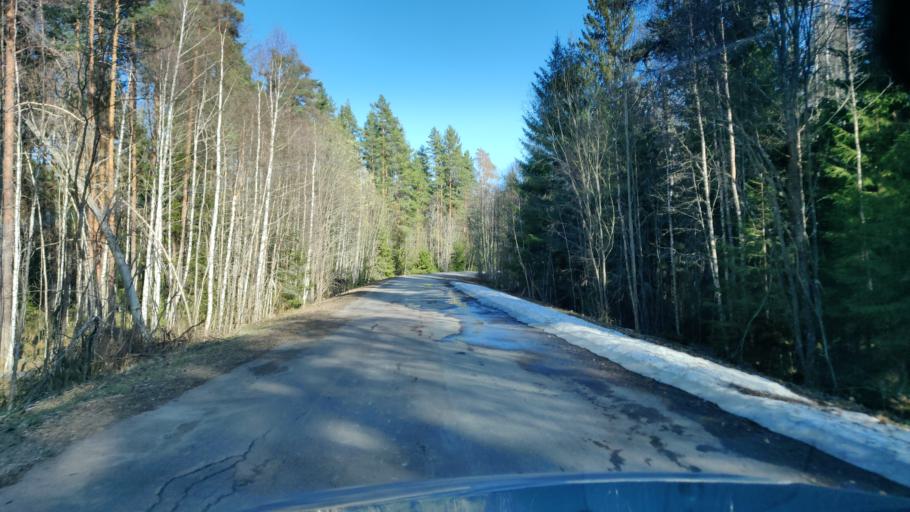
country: SE
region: Vaermland
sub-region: Hagfors Kommun
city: Hagfors
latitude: 59.9731
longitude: 13.5500
